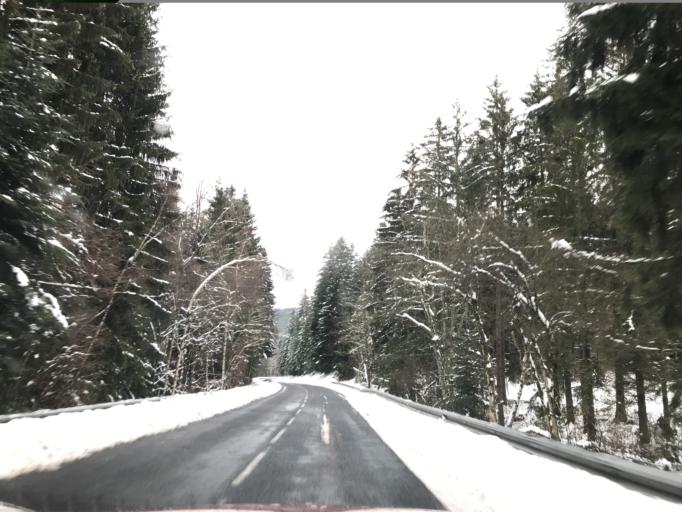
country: FR
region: Auvergne
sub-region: Departement du Puy-de-Dome
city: Celles-sur-Durolle
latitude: 45.7641
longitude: 3.6704
